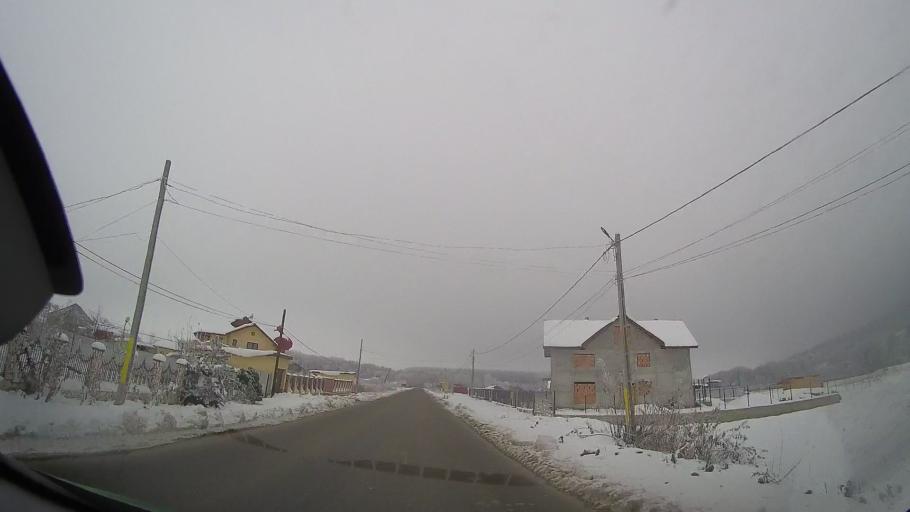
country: RO
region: Neamt
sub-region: Comuna Horia
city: Cotu Vames
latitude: 46.8765
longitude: 26.9762
